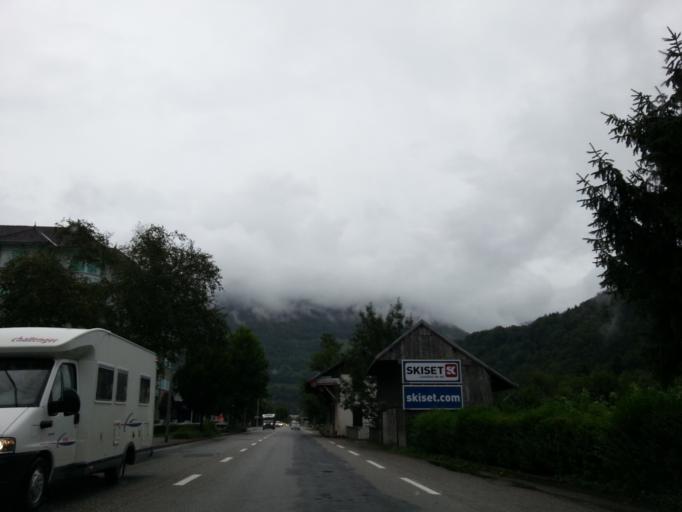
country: FR
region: Rhone-Alpes
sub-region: Departement de la Savoie
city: Ugine
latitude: 45.7501
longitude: 6.4093
